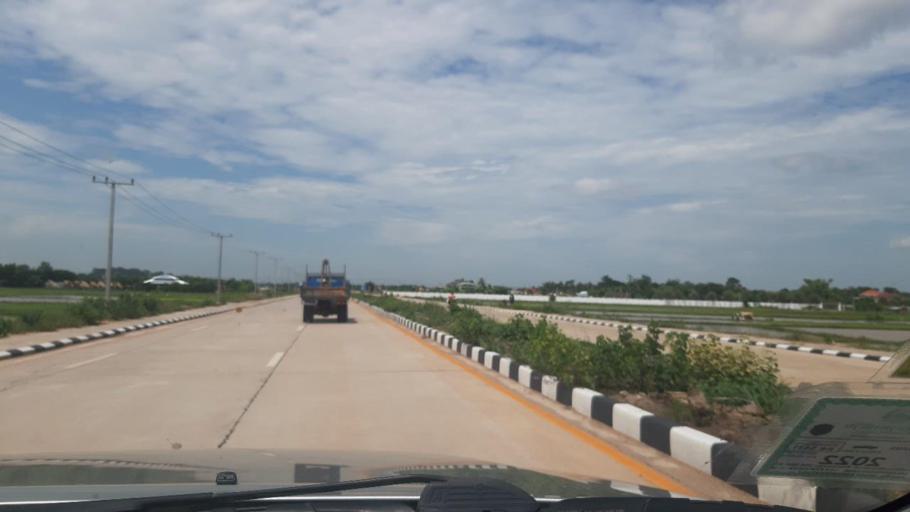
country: LA
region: Vientiane
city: Vientiane
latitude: 18.0360
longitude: 102.6123
